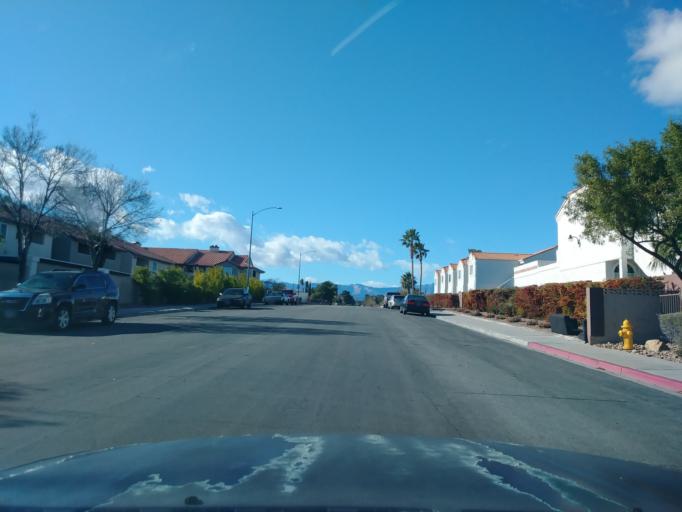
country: US
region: Nevada
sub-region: Clark County
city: Spring Valley
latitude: 36.1500
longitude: -115.2112
